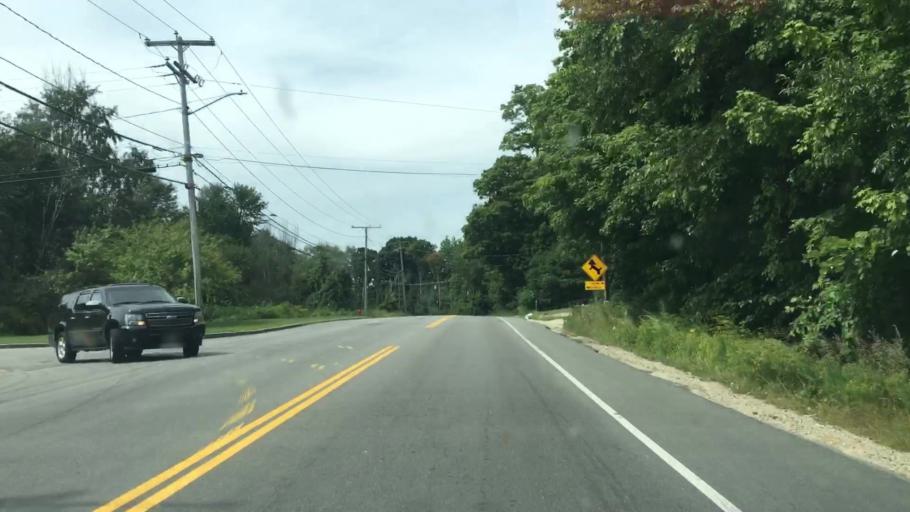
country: US
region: New Hampshire
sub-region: Strafford County
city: Madbury
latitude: 43.1885
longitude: -70.9152
